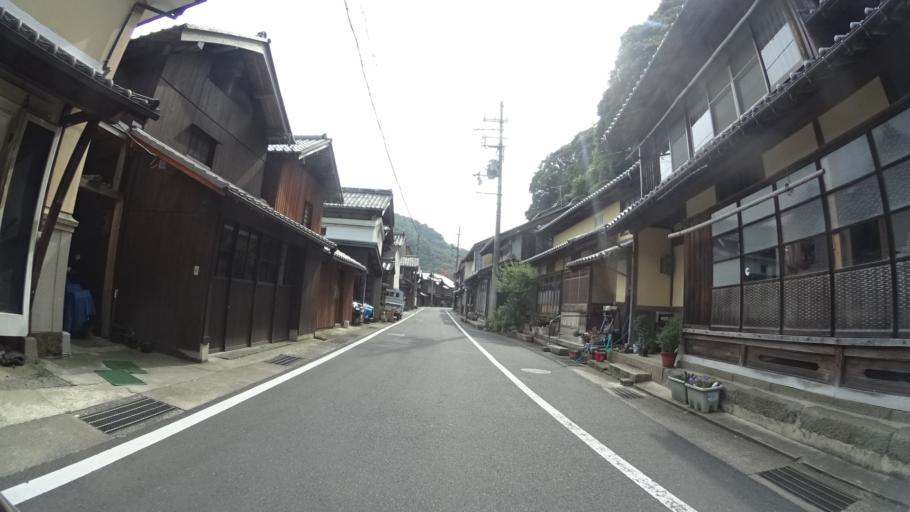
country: JP
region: Kyoto
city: Miyazu
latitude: 35.6701
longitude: 135.2797
